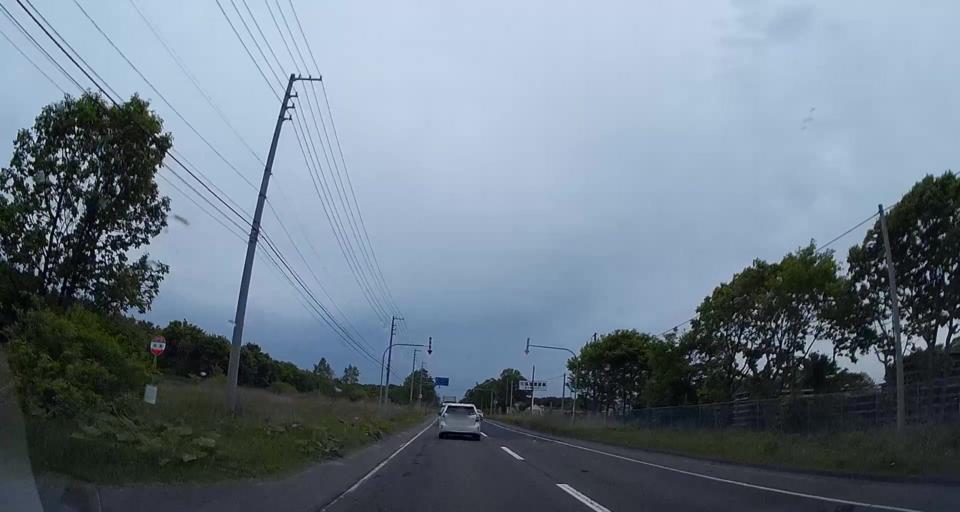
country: JP
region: Hokkaido
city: Chitose
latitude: 42.7153
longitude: 141.7539
